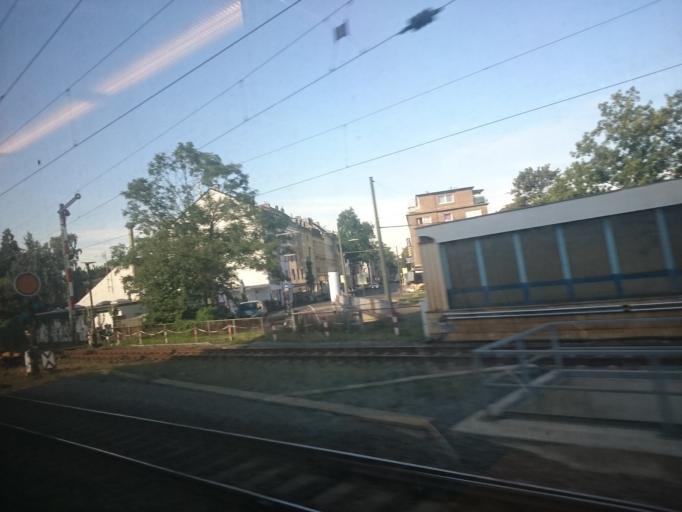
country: DE
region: North Rhine-Westphalia
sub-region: Regierungsbezirk Dusseldorf
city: Ratingen
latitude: 51.2639
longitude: 6.8210
